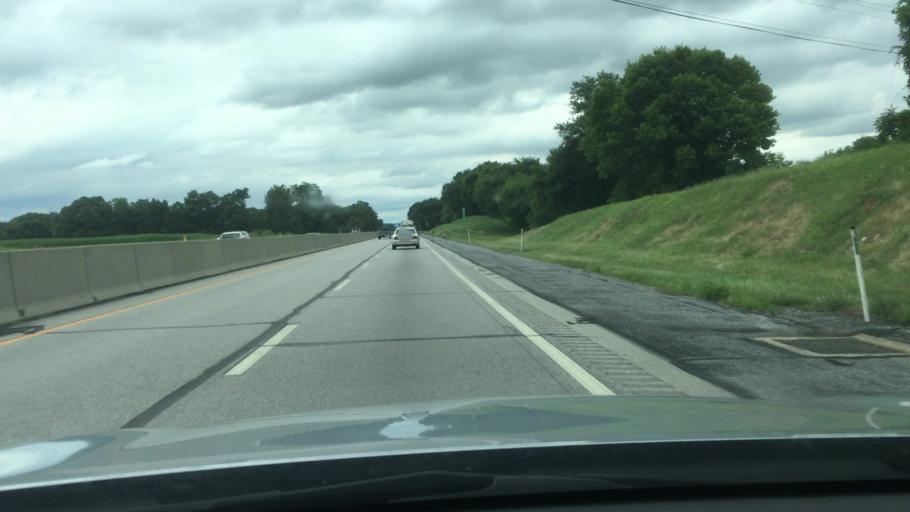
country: US
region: Pennsylvania
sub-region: Cumberland County
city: Mechanicsburg
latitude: 40.1976
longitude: -77.0263
